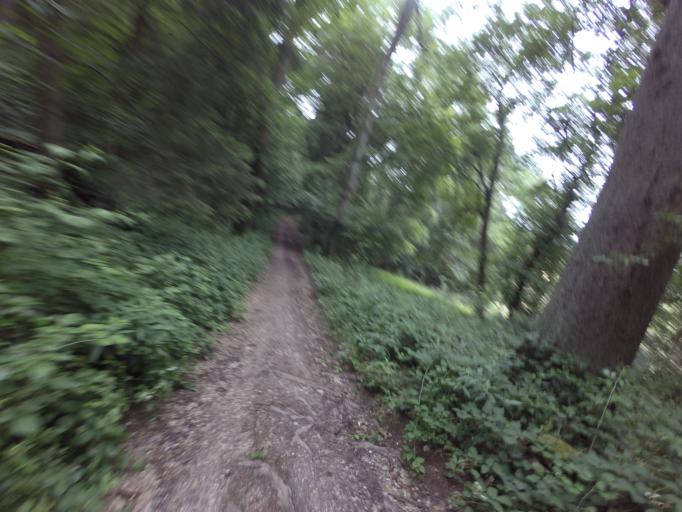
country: BE
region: Wallonia
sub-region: Province de Liege
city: Plombieres
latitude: 50.7582
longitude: 5.9816
